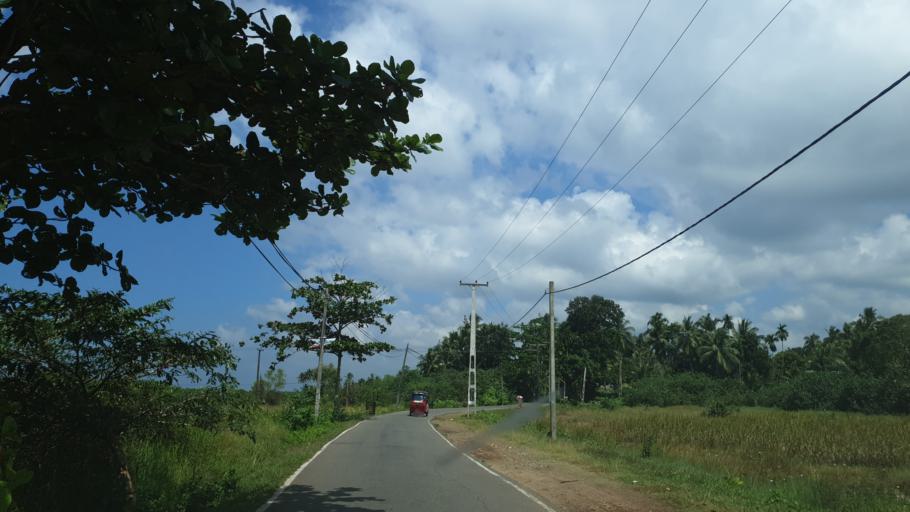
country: LK
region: Western
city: Panadura
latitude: 6.6783
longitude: 79.9397
